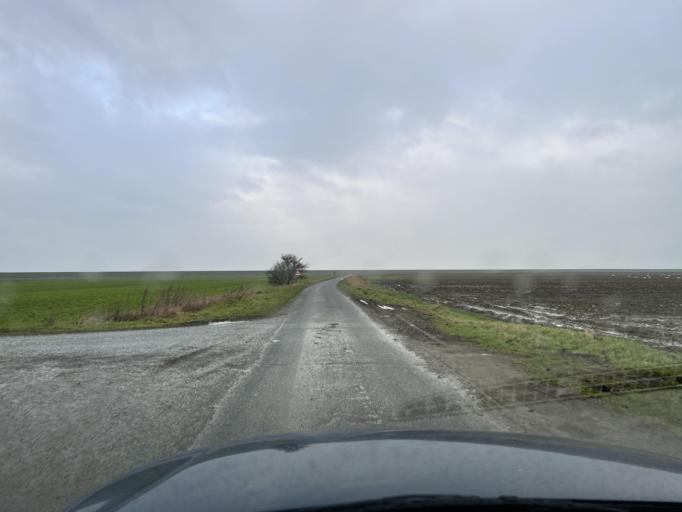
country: DE
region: Schleswig-Holstein
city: Hellschen-Heringsand-Unterschaar
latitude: 54.2218
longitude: 8.8524
